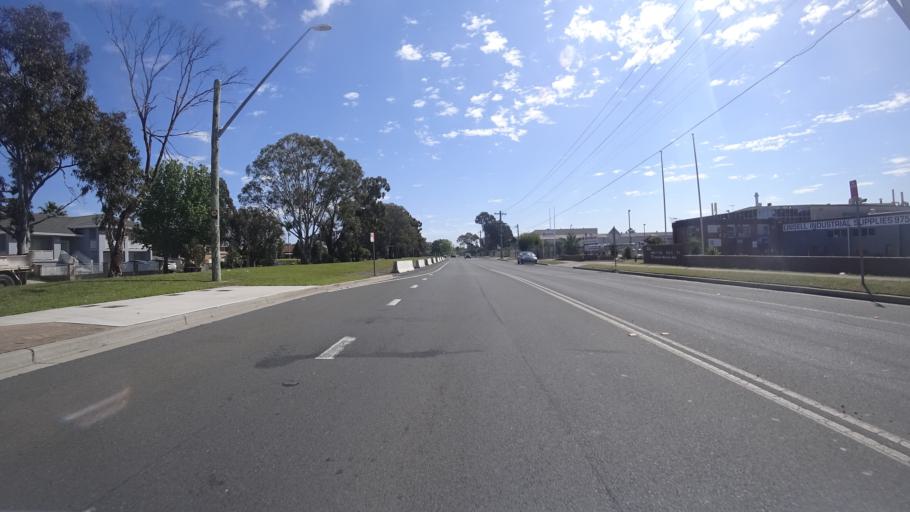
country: AU
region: New South Wales
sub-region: Fairfield
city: Chipping Norton
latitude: -33.9184
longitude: 150.9617
